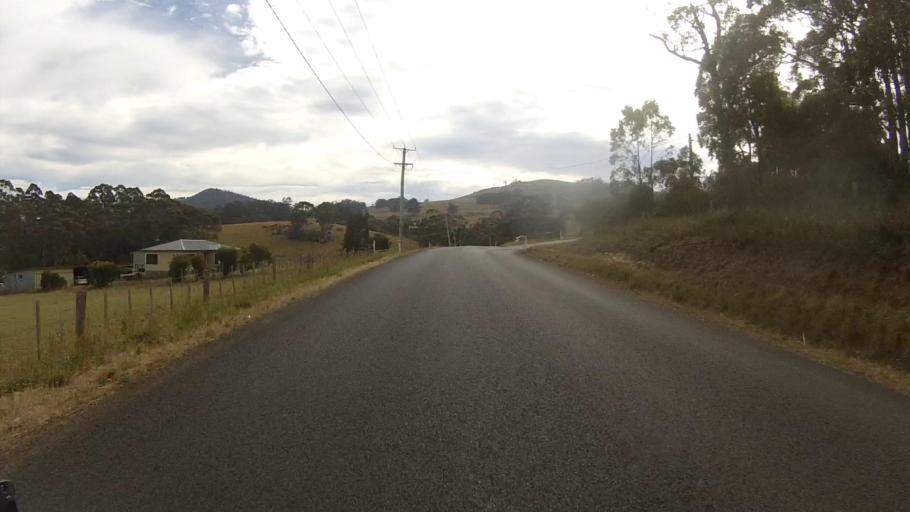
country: AU
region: Tasmania
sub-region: Sorell
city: Sorell
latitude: -42.7895
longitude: 147.8029
